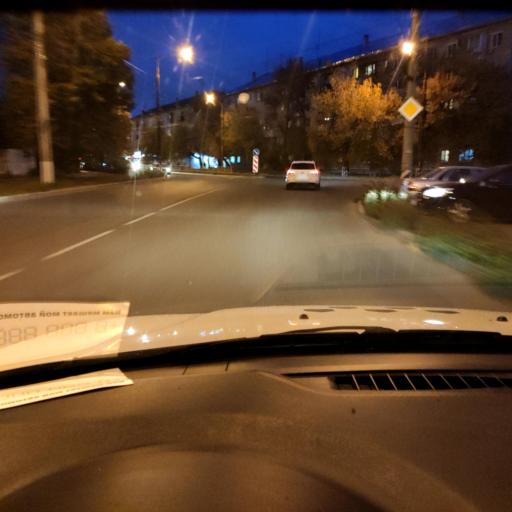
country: RU
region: Samara
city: Tol'yatti
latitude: 53.5222
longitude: 49.4194
